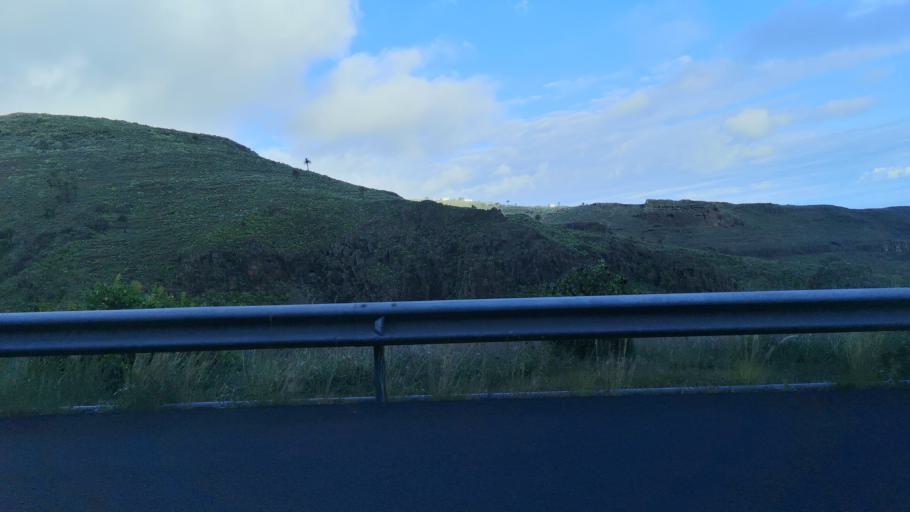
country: ES
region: Canary Islands
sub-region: Provincia de Santa Cruz de Tenerife
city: Alajero
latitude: 28.0688
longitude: -17.2066
